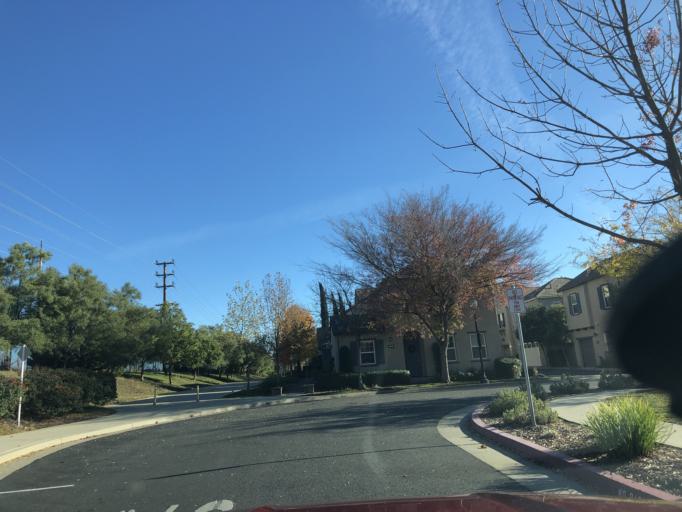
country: US
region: California
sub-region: Placer County
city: Roseville
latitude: 38.7840
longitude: -121.2890
